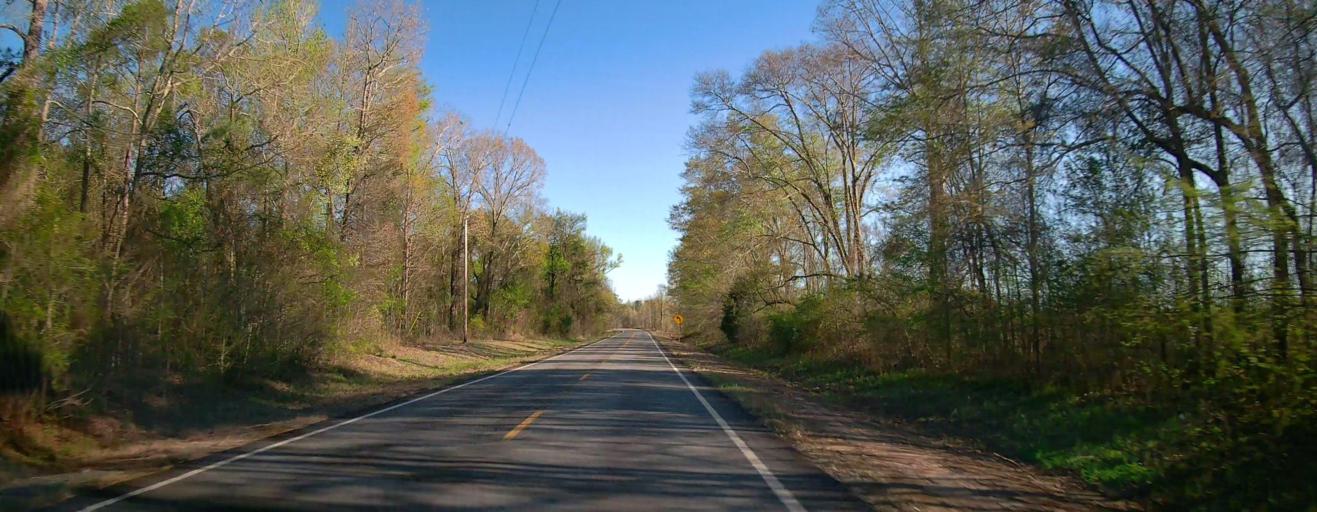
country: US
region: Georgia
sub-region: Baldwin County
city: Hardwick
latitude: 32.9538
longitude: -83.1661
